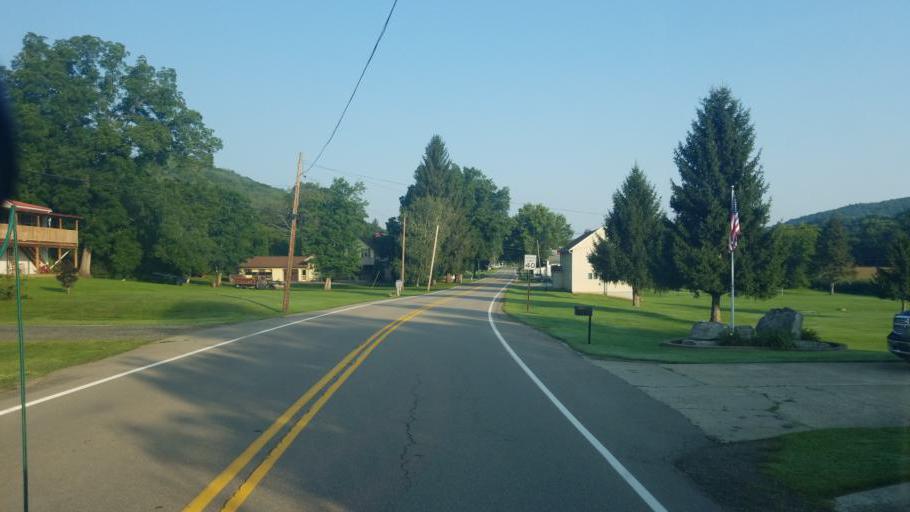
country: US
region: Pennsylvania
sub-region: Tioga County
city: Westfield
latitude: 41.9933
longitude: -77.4952
